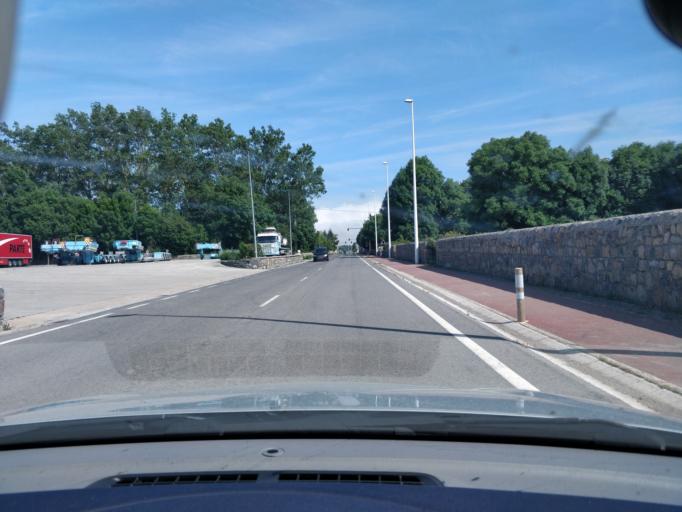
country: ES
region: Cantabria
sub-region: Provincia de Cantabria
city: Reinosa
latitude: 43.0092
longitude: -4.1699
